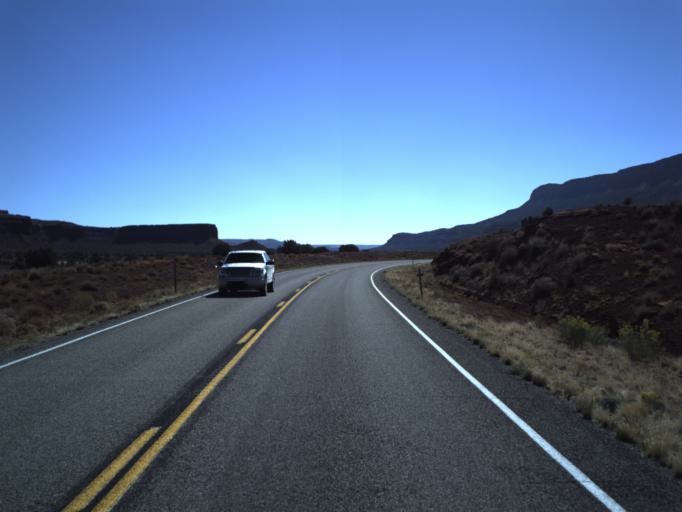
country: US
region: Utah
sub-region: San Juan County
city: Blanding
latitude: 37.7006
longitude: -110.2335
